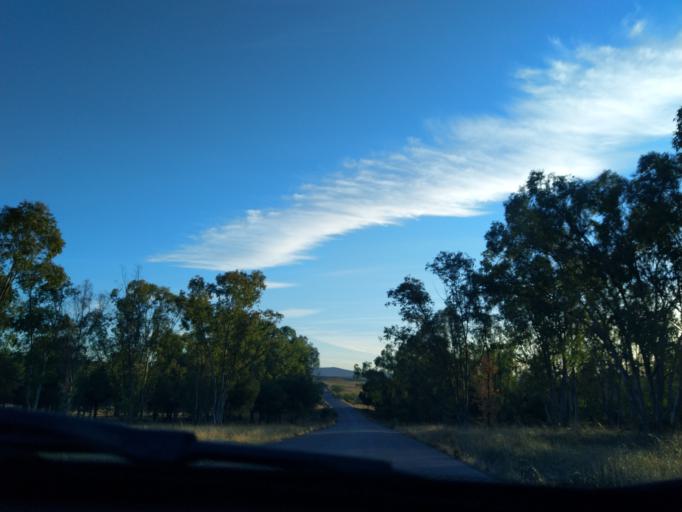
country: ES
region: Extremadura
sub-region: Provincia de Badajoz
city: Berlanga
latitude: 38.2716
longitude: -5.8215
